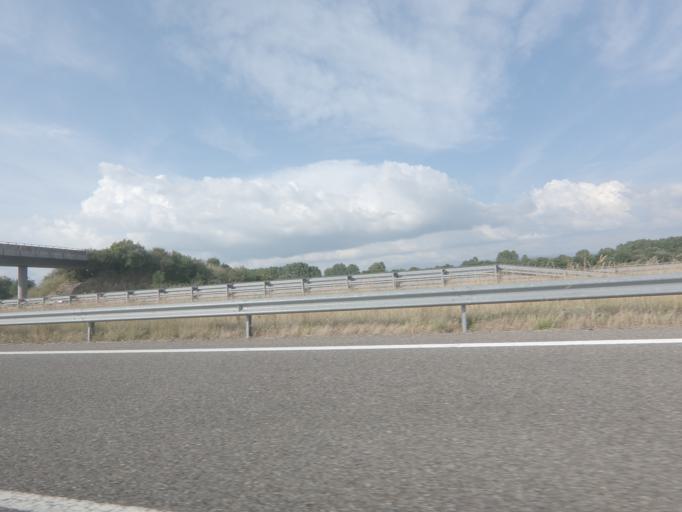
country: ES
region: Galicia
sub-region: Provincia de Ourense
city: Xinzo de Limia
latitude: 42.0847
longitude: -7.7178
